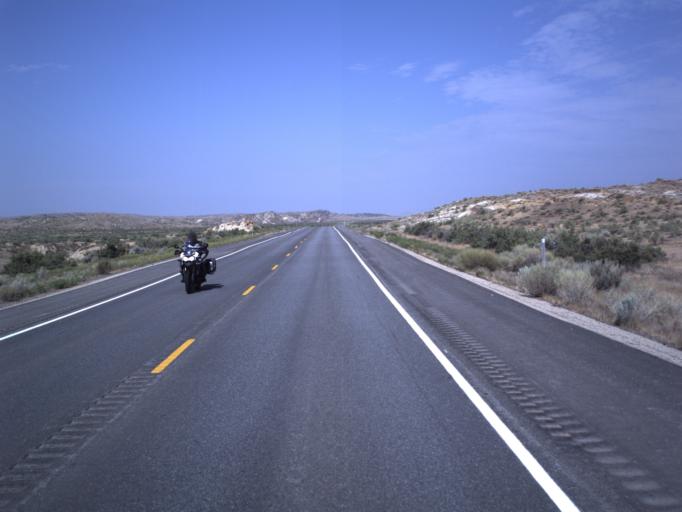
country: US
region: Colorado
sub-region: Rio Blanco County
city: Rangely
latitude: 40.2856
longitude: -109.1265
